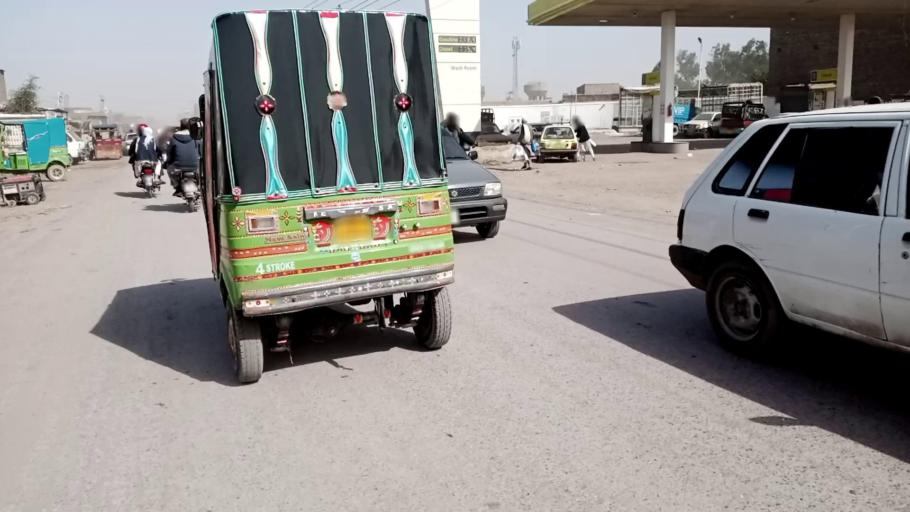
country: PK
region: Khyber Pakhtunkhwa
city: Peshawar
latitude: 33.9897
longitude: 71.6334
